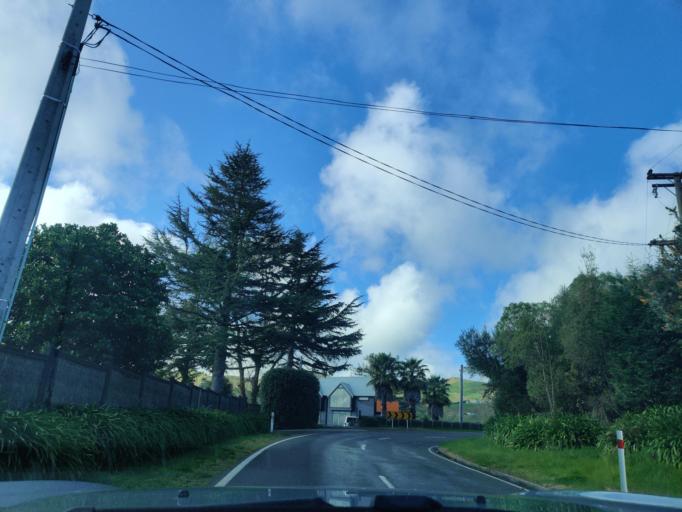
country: NZ
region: Hawke's Bay
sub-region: Hastings District
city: Hastings
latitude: -39.6830
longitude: 176.8984
